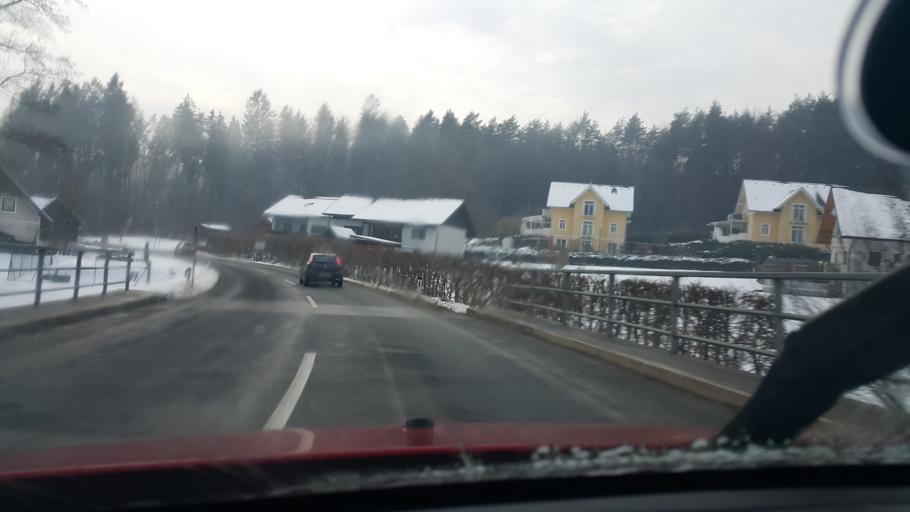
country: AT
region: Styria
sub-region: Politischer Bezirk Graz-Umgebung
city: Hitzendorf
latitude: 47.0646
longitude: 15.3021
